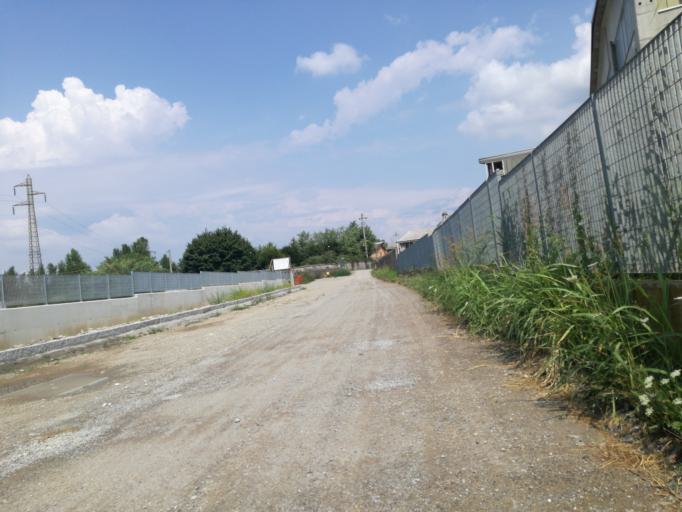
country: IT
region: Lombardy
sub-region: Provincia di Bergamo
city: Calusco d'Adda
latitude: 45.6826
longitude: 9.4738
